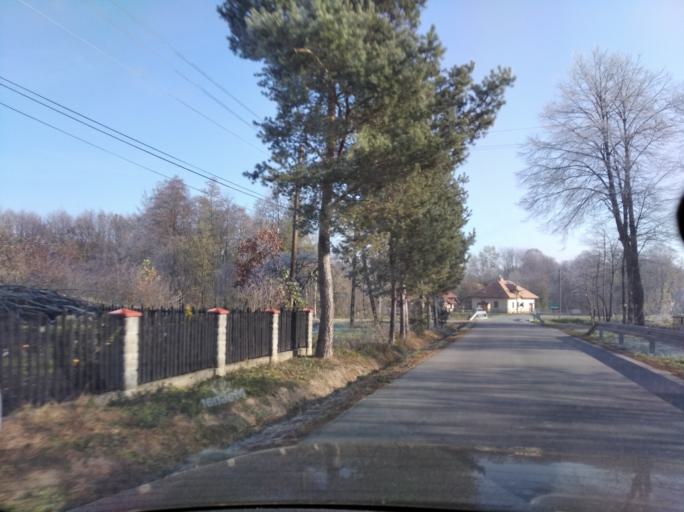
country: PL
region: Subcarpathian Voivodeship
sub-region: Powiat strzyzowski
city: Wysoka Strzyzowska
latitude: 49.8349
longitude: 21.7211
